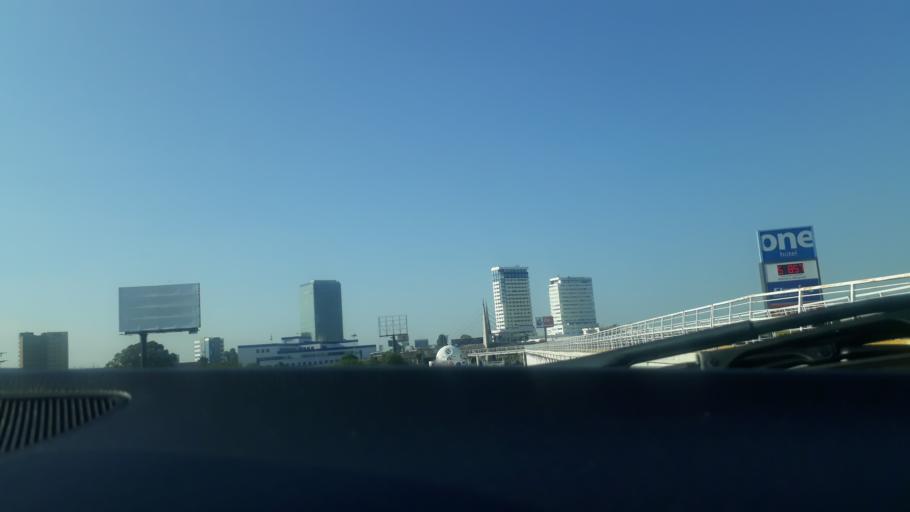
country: MX
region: Puebla
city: Tlazcalancingo
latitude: 19.0134
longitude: -98.2637
